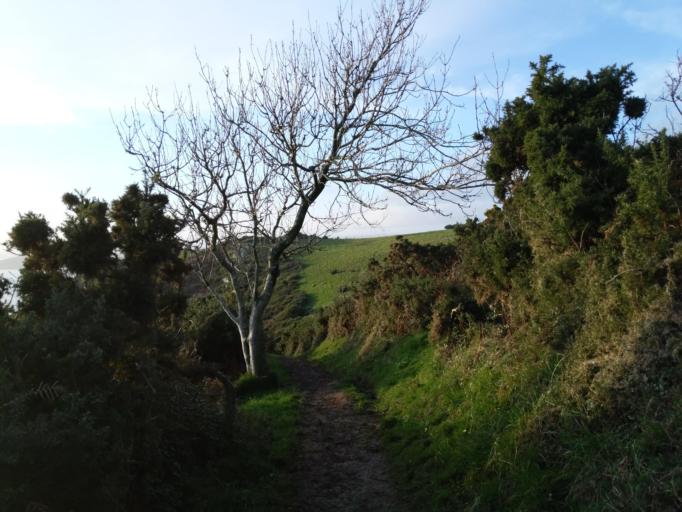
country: GB
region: England
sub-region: Cornwall
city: Fowey
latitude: 50.3256
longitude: -4.6217
